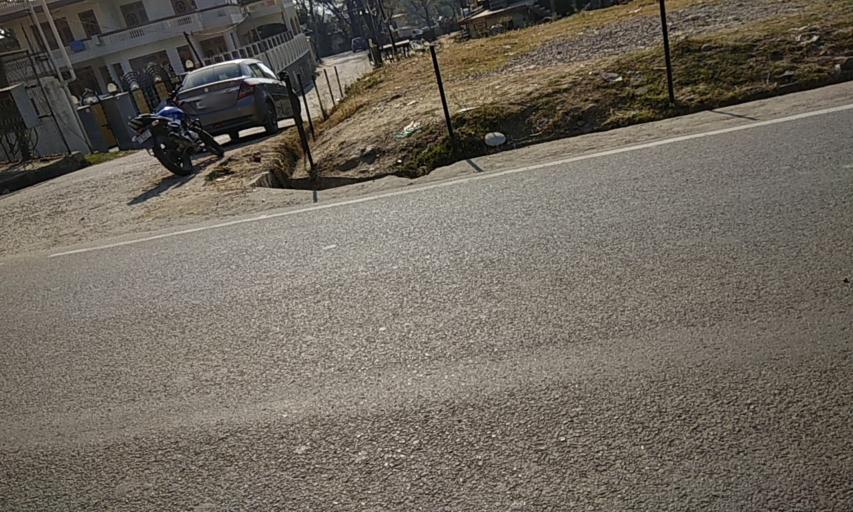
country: IN
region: Himachal Pradesh
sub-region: Kangra
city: Palampur
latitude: 32.1130
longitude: 76.5295
